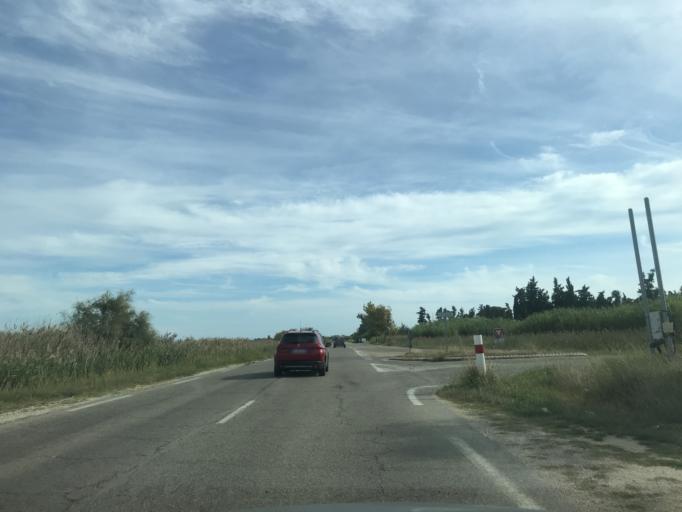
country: FR
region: Provence-Alpes-Cote d'Azur
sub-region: Departement des Bouches-du-Rhone
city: Saintes-Maries-de-la-Mer
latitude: 43.5331
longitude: 4.3745
